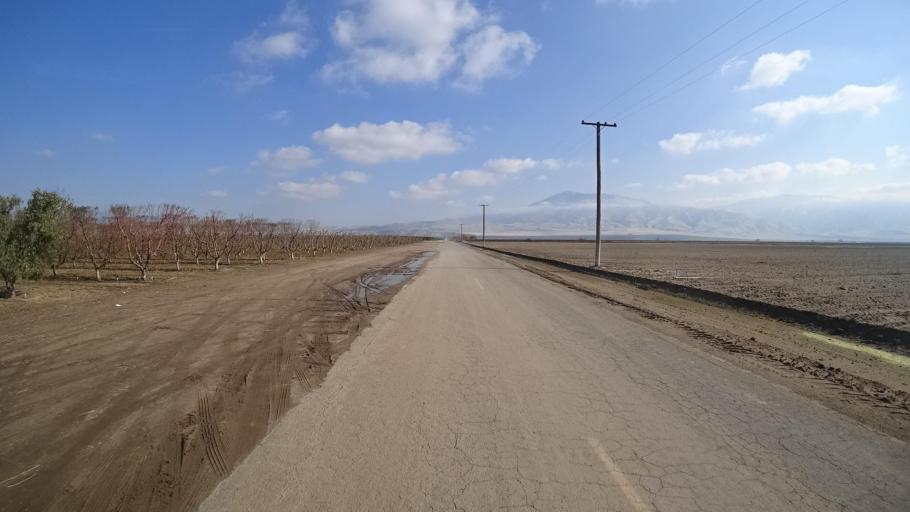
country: US
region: California
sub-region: Kern County
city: Arvin
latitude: 35.2530
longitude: -118.8000
